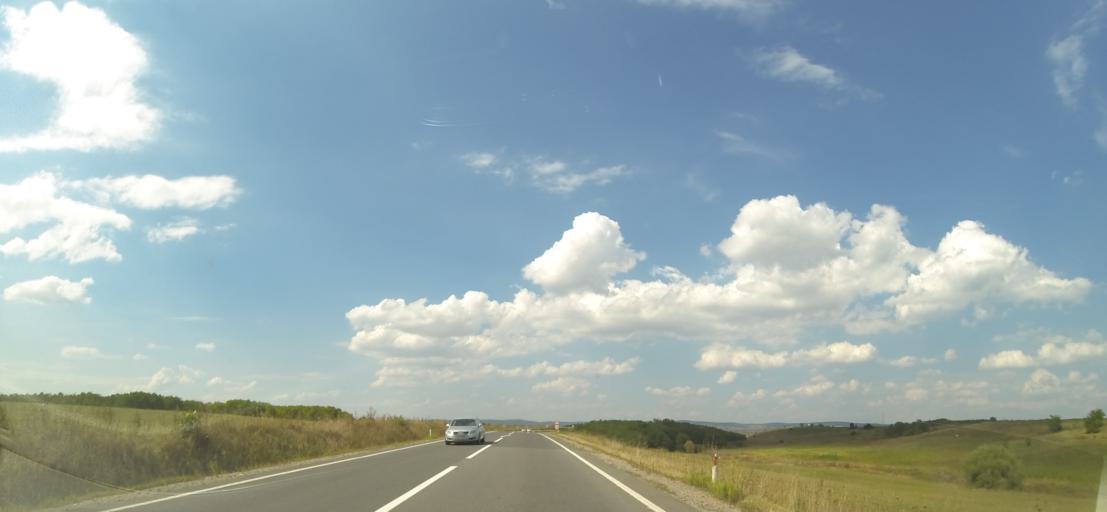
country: RO
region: Brasov
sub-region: Comuna Sercaia
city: Sercaia
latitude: 45.8183
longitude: 25.1607
